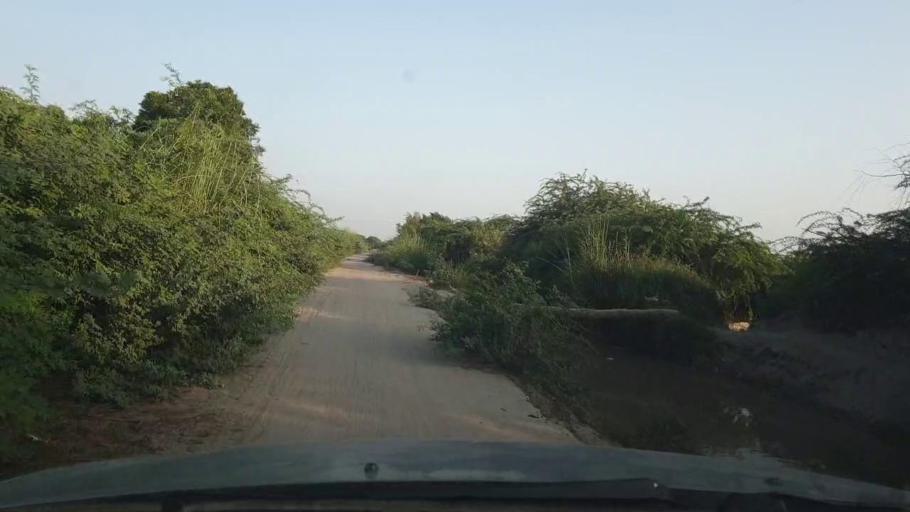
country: PK
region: Sindh
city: Tando Ghulam Ali
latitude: 25.1487
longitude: 68.9693
